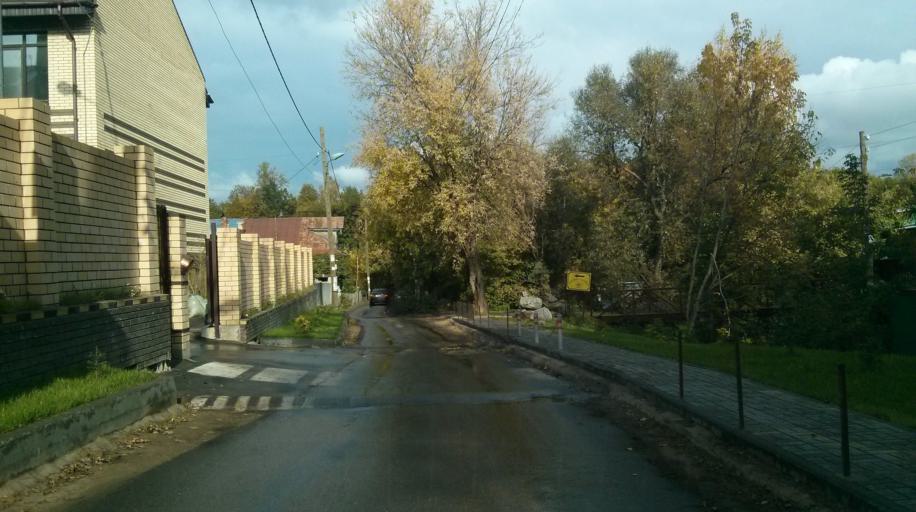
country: RU
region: Nizjnij Novgorod
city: Nizhniy Novgorod
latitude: 56.3064
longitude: 44.0439
